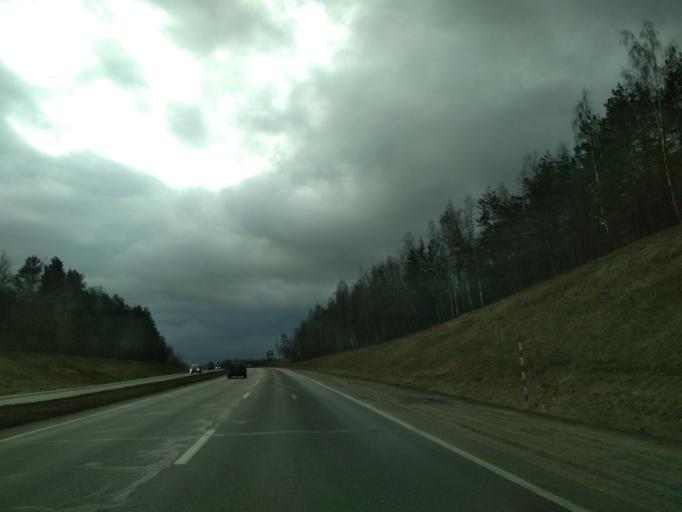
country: BY
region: Minsk
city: Luhavaya Slabada
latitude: 53.7667
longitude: 27.8274
